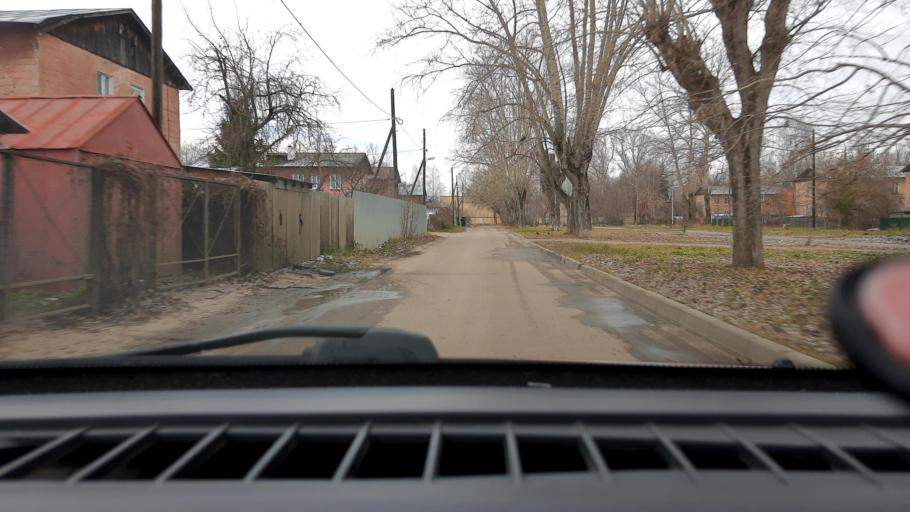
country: RU
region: Nizjnij Novgorod
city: Gorbatovka
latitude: 56.3810
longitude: 43.7862
